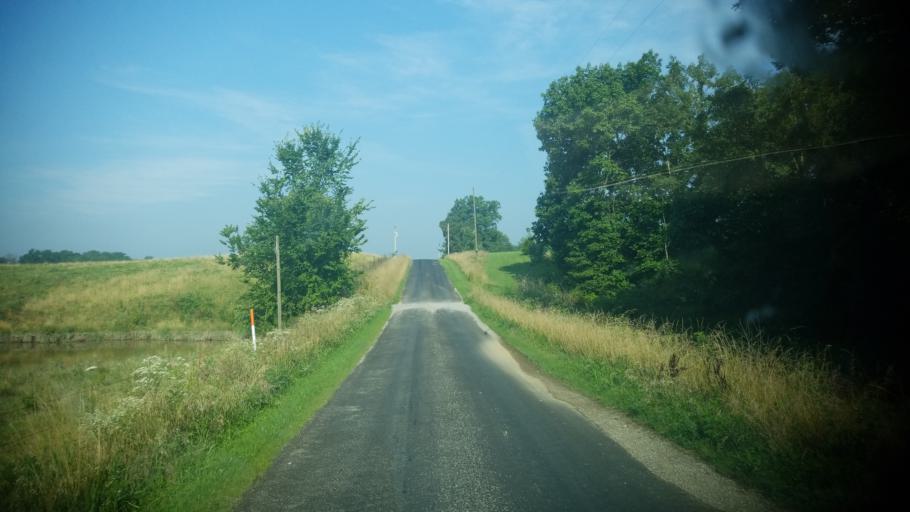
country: US
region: Illinois
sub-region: Clay County
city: Flora
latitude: 38.6026
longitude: -88.3891
